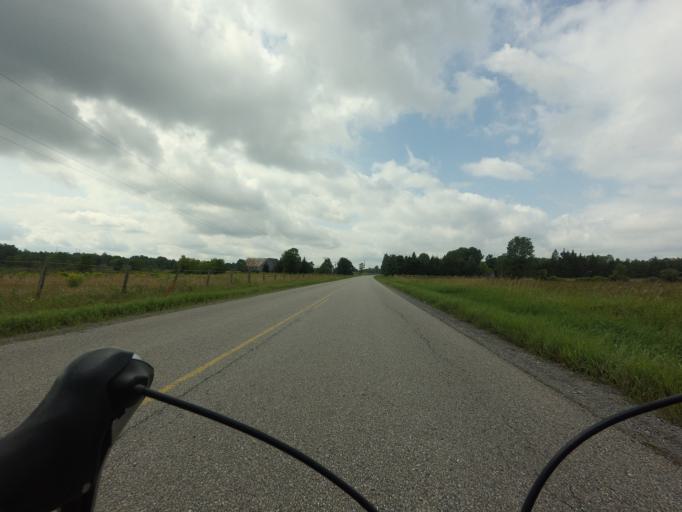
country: CA
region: Ontario
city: Brockville
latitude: 44.7772
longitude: -75.7253
